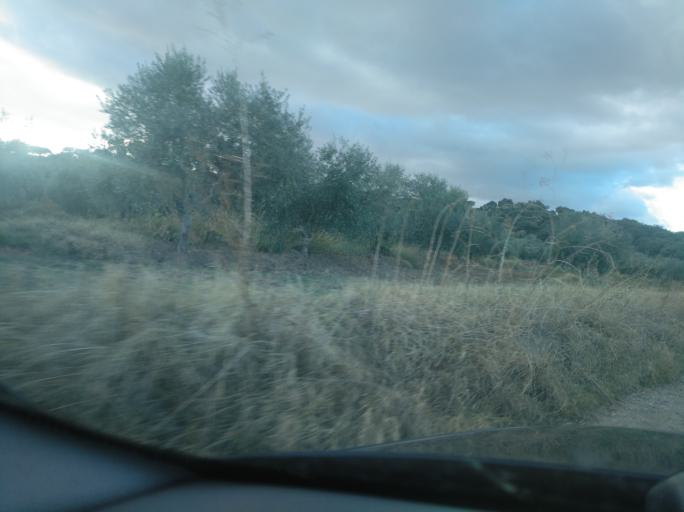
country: PT
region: Portalegre
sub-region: Campo Maior
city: Campo Maior
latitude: 39.0451
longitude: -6.9952
